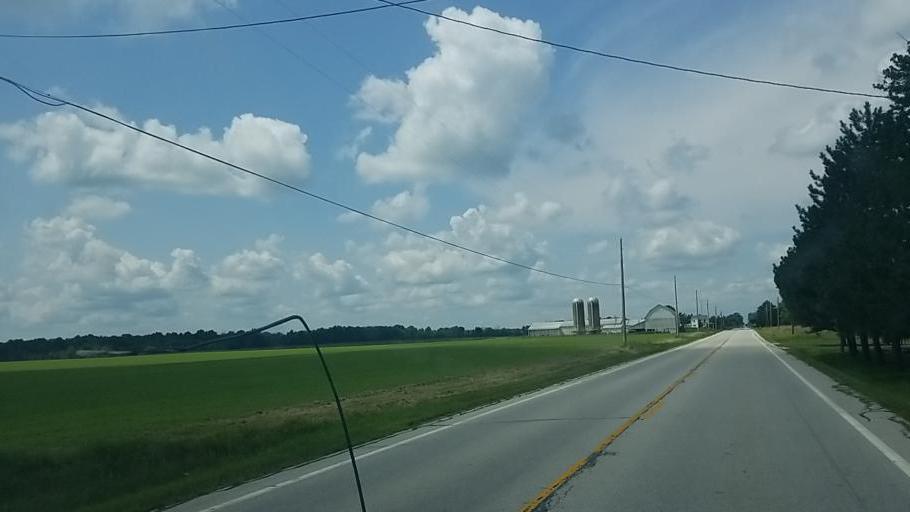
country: US
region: Ohio
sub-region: Wayne County
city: West Salem
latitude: 41.0270
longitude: -82.1009
